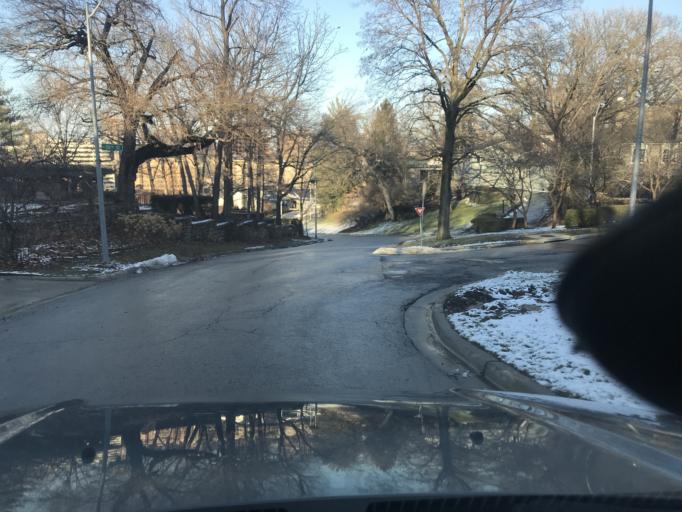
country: US
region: Kansas
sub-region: Johnson County
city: Westwood
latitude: 39.0369
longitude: -94.5965
